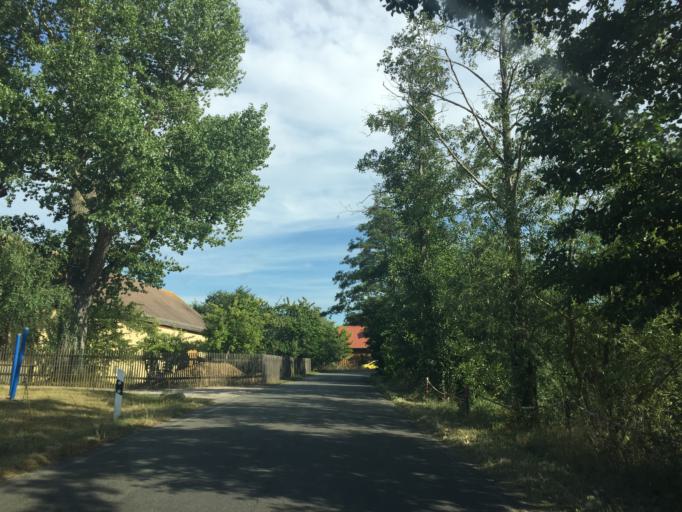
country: DE
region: Thuringia
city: Schmolln
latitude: 50.8760
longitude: 12.3713
